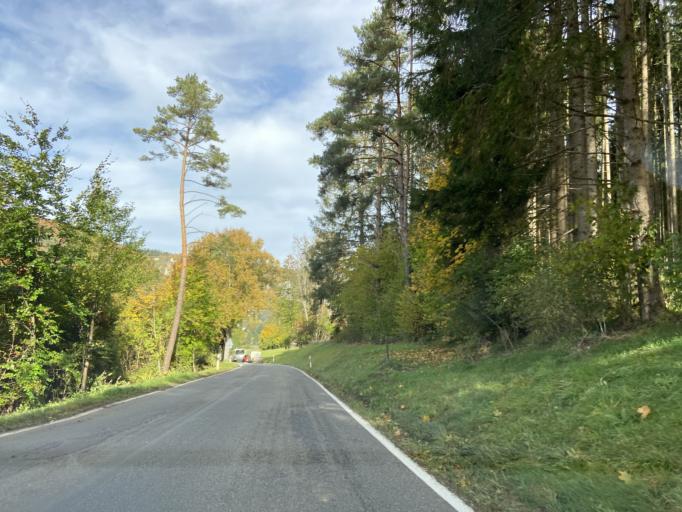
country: DE
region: Baden-Wuerttemberg
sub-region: Tuebingen Region
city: Leibertingen
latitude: 48.0761
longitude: 9.0343
